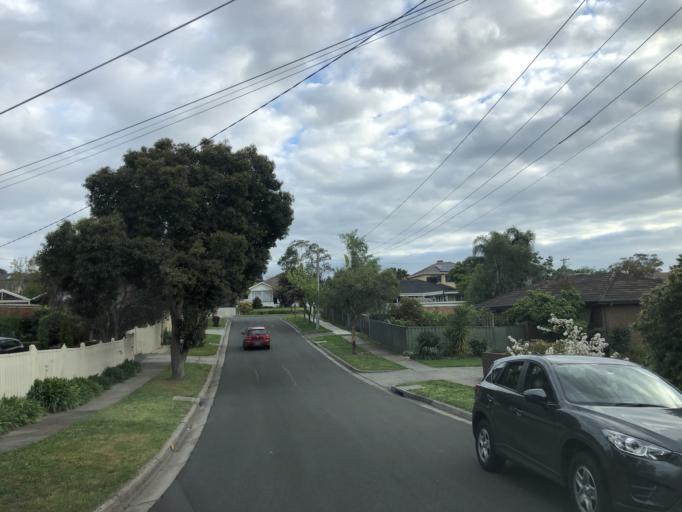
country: AU
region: Victoria
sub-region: Whitehorse
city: Burwood
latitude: -37.8609
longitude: 145.1188
